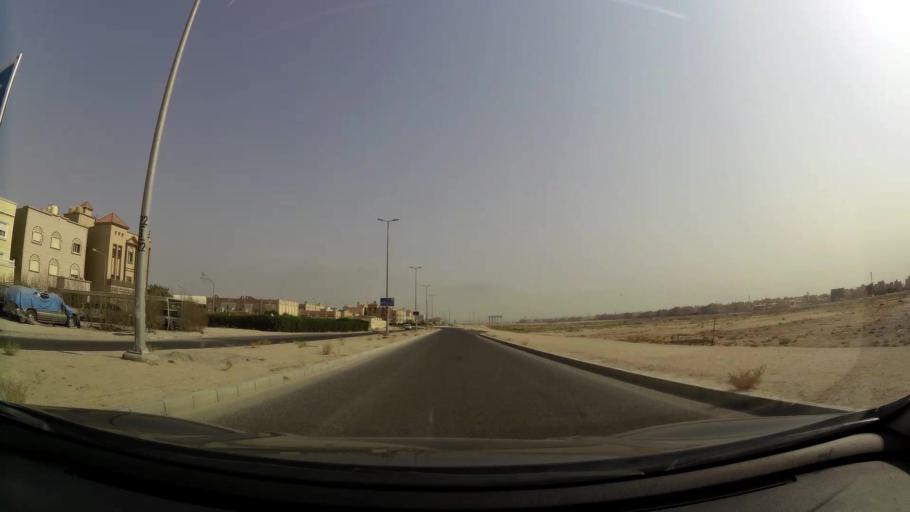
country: KW
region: Muhafazat al Jahra'
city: Al Jahra'
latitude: 29.3316
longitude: 47.7625
